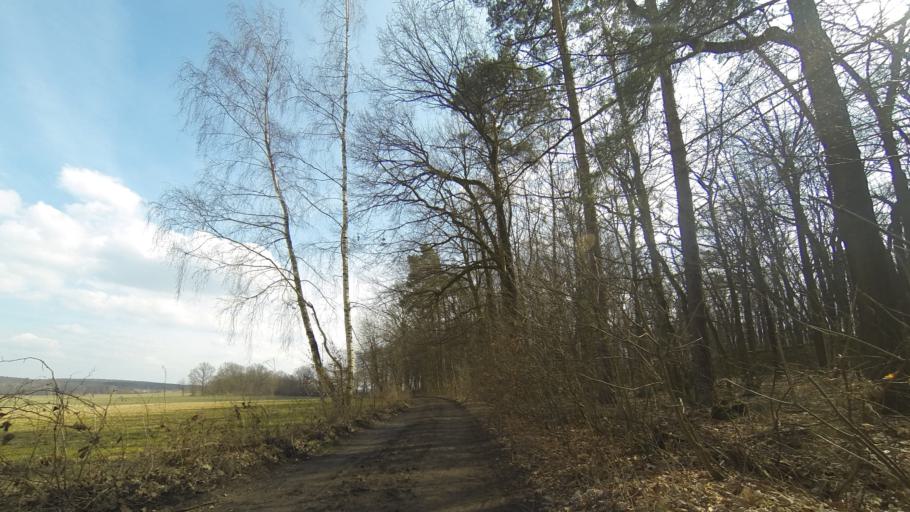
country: DE
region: Saxony
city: Moritzburg
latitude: 51.1734
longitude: 13.7037
